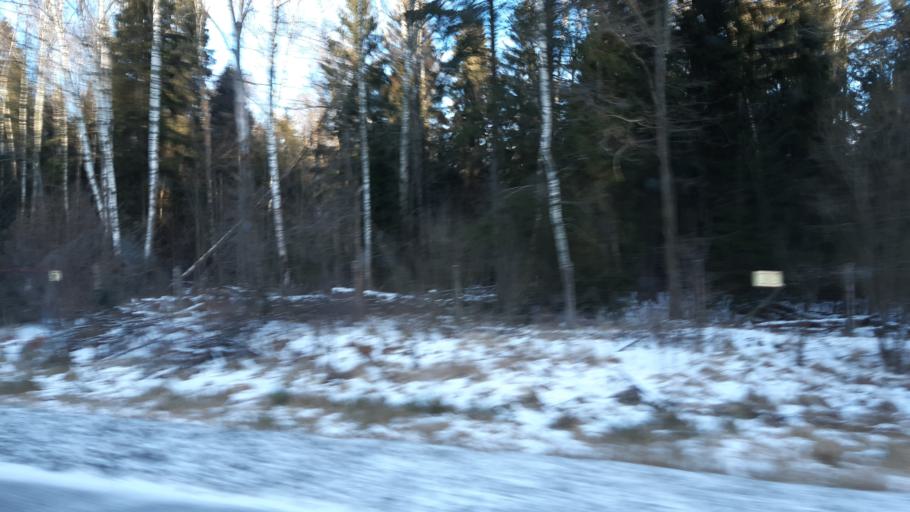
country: RU
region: Vladimir
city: Arsaki
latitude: 56.2772
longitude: 38.4077
